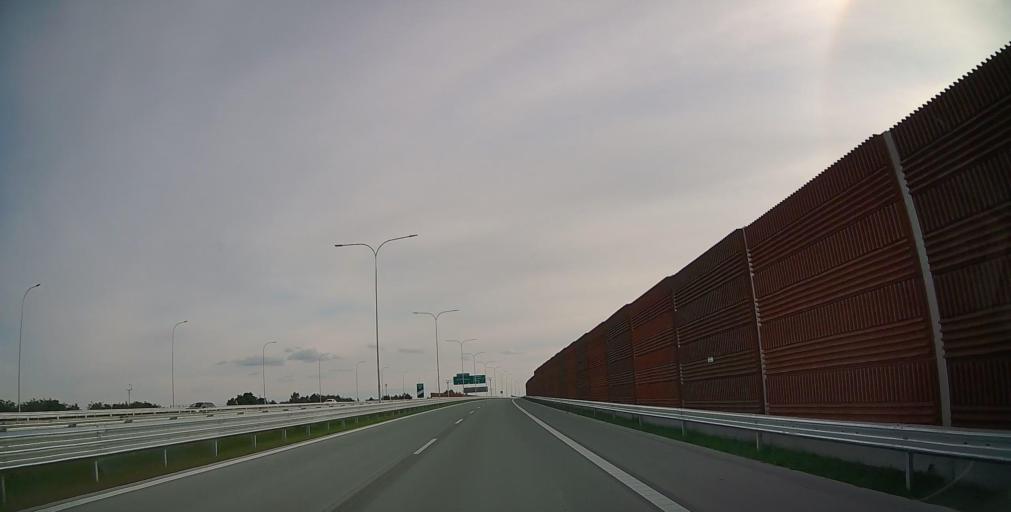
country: PL
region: Masovian Voivodeship
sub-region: Powiat piaseczynski
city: Mysiadlo
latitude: 52.1316
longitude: 20.9897
